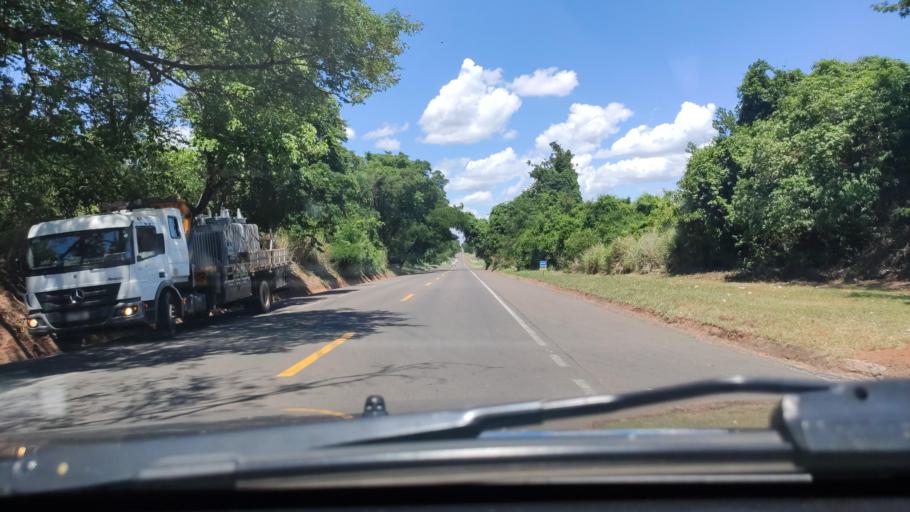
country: BR
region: Sao Paulo
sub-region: Boa Esperanca Do Sul
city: Boa Esperanca do Sul
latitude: -22.0691
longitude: -48.3788
